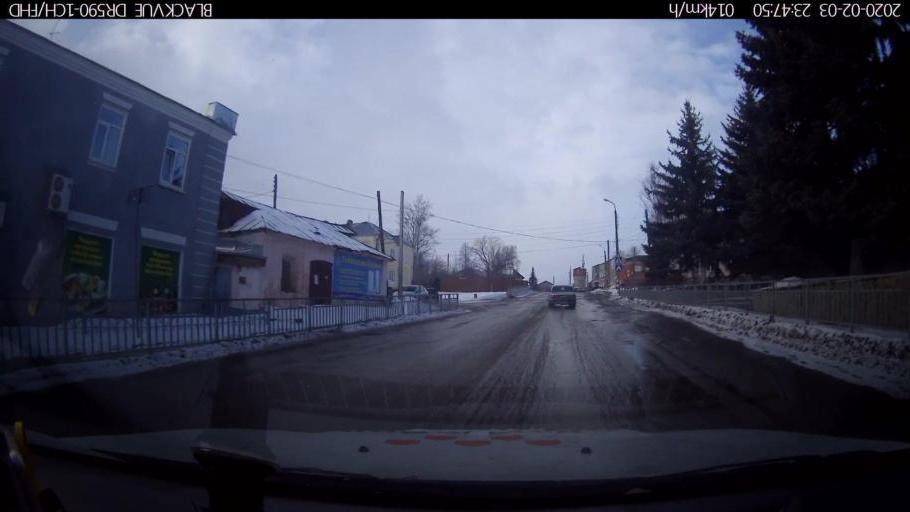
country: RU
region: Nizjnij Novgorod
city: Dal'neye Konstantinovo
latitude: 55.8108
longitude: 44.0966
